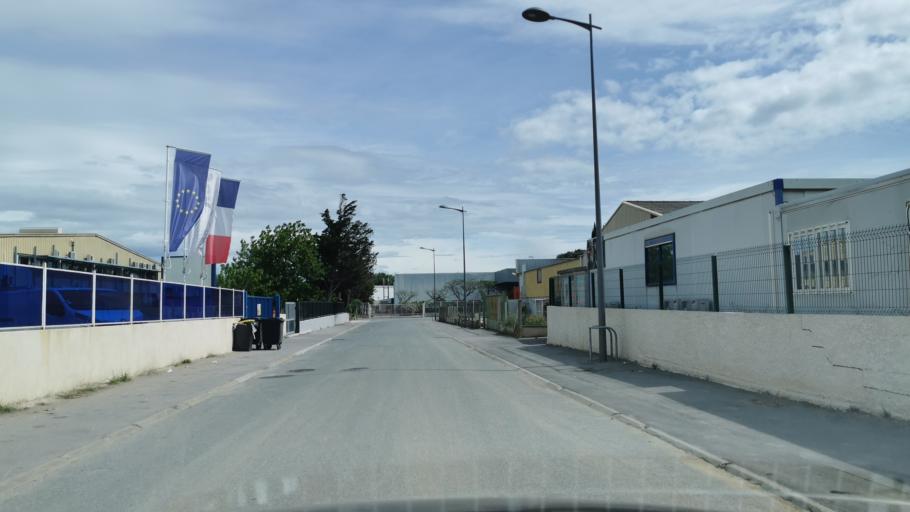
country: FR
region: Languedoc-Roussillon
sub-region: Departement de l'Aude
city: Narbonne
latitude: 43.1745
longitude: 2.9848
